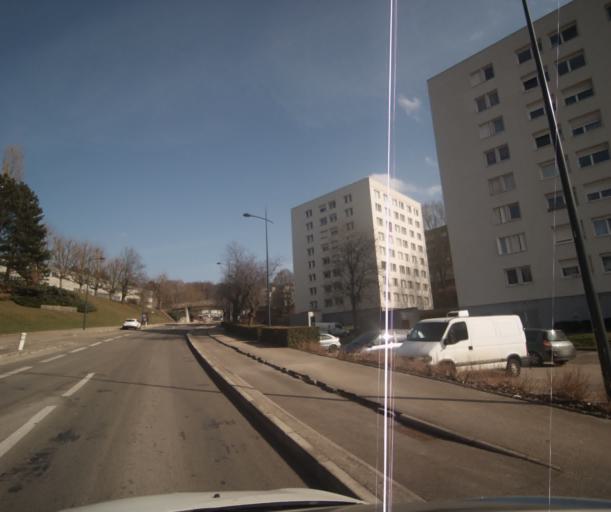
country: FR
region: Franche-Comte
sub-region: Departement du Doubs
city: Montfaucon
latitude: 47.2508
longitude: 6.0571
